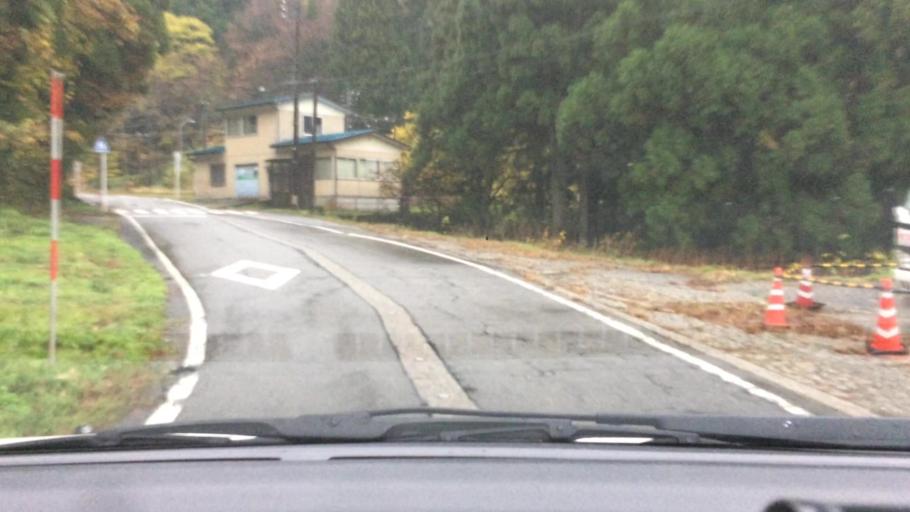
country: JP
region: Toyama
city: Kamiichi
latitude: 36.5742
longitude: 137.3862
